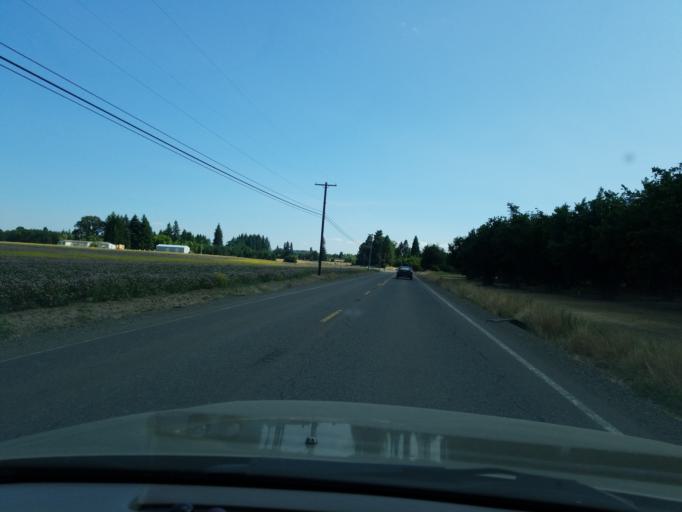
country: US
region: Oregon
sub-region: Yamhill County
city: Carlton
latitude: 45.2637
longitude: -123.2046
